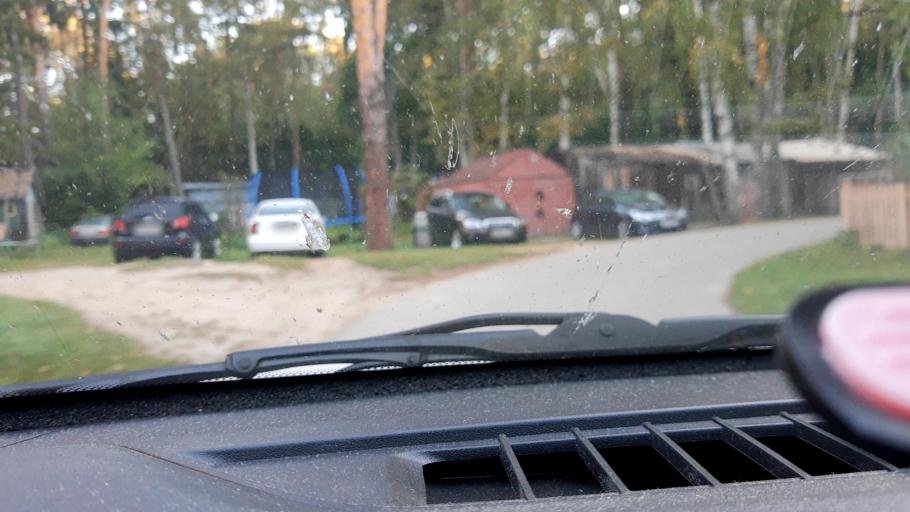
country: RU
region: Nizjnij Novgorod
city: Kstovo
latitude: 56.1702
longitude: 44.1278
